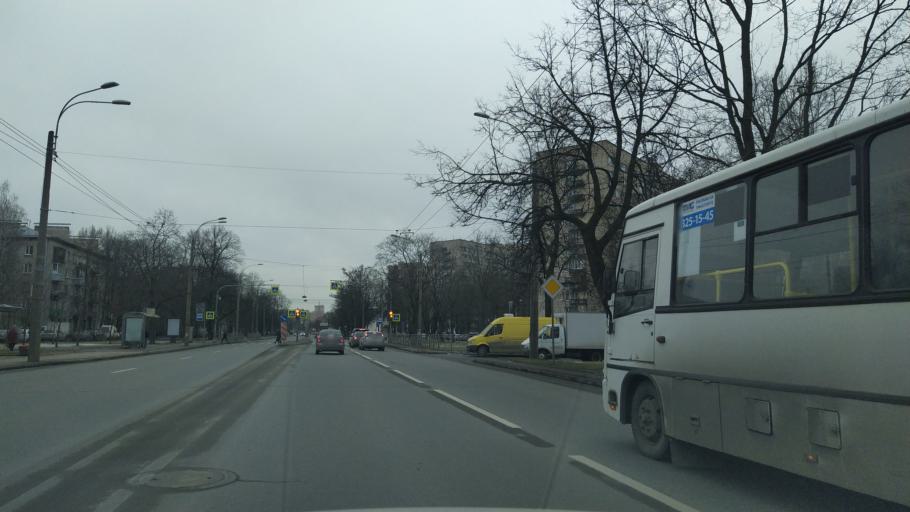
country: RU
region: St.-Petersburg
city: Kushelevka
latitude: 60.0031
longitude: 30.3590
